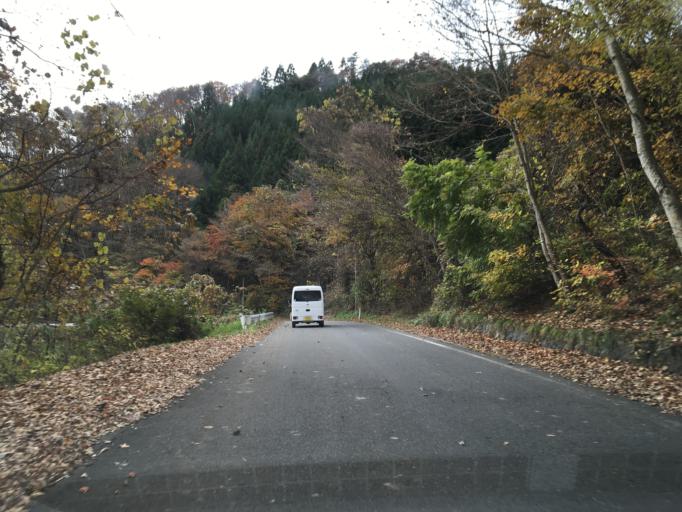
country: JP
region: Iwate
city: Mizusawa
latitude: 39.0898
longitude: 141.3468
